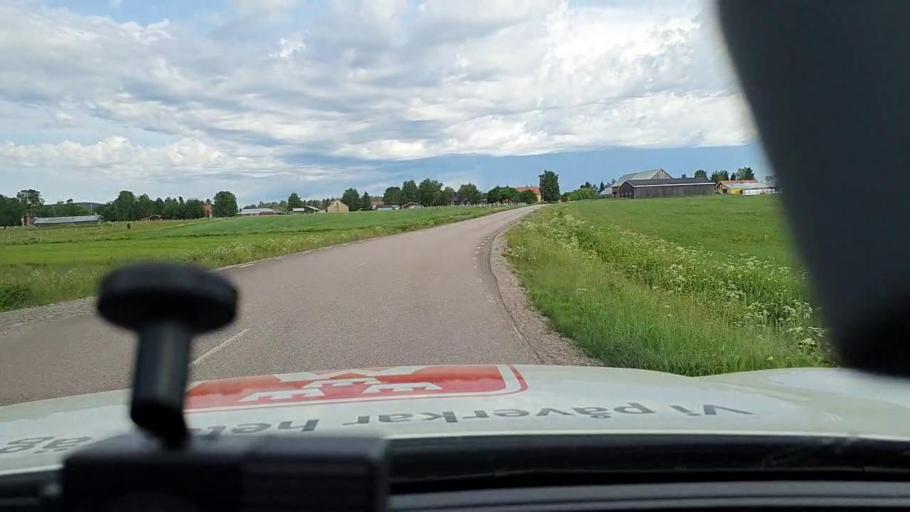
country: SE
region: Norrbotten
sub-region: Bodens Kommun
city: Saevast
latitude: 65.7064
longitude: 21.7626
